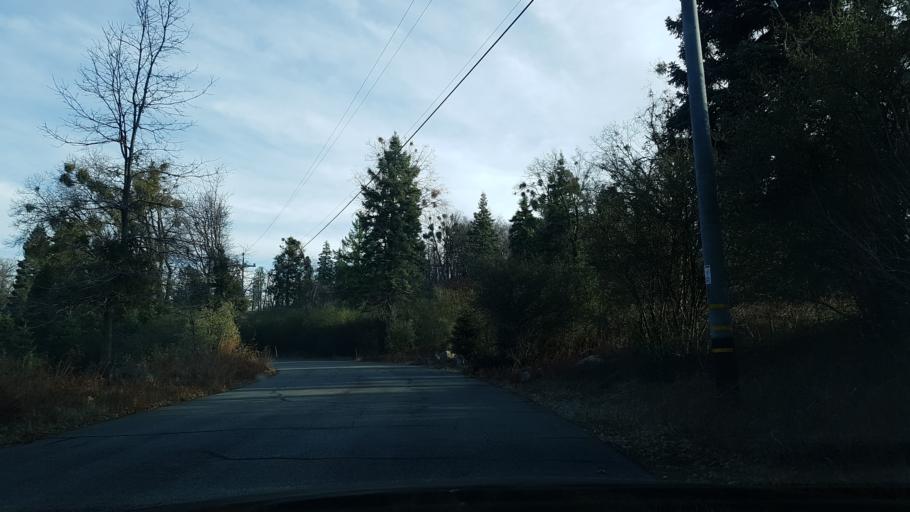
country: US
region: California
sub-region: Riverside County
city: Aguanga
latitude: 33.3299
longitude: -116.9017
